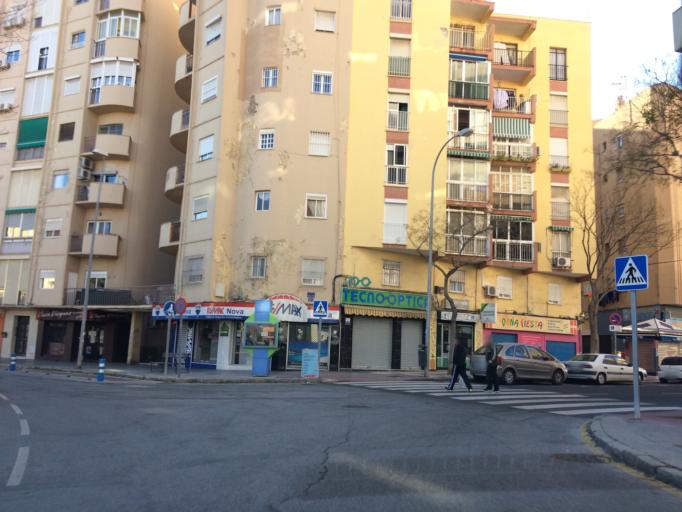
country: ES
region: Andalusia
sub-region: Provincia de Malaga
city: Malaga
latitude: 36.7218
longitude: -4.4400
